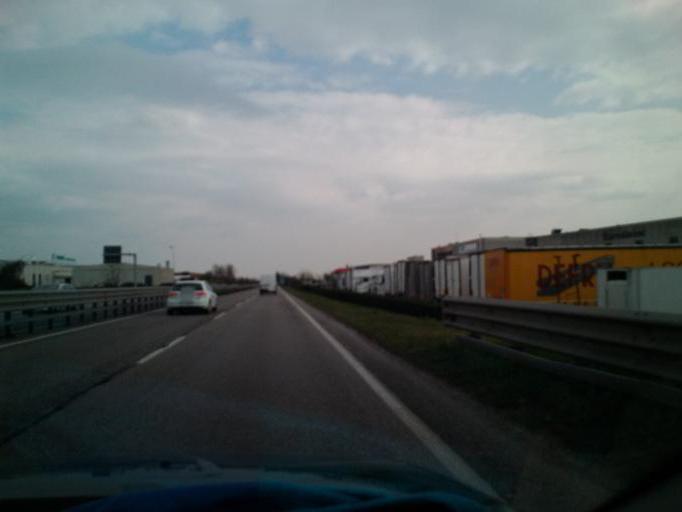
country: IT
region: Veneto
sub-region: Provincia di Verona
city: Bassone
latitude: 45.4543
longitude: 10.8815
